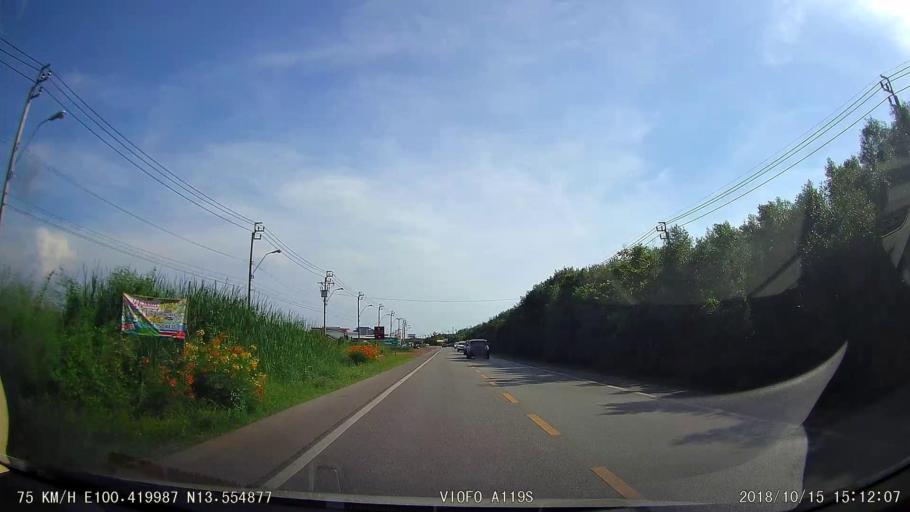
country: TH
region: Bangkok
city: Bang Khun Thian
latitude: 13.5549
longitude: 100.4200
